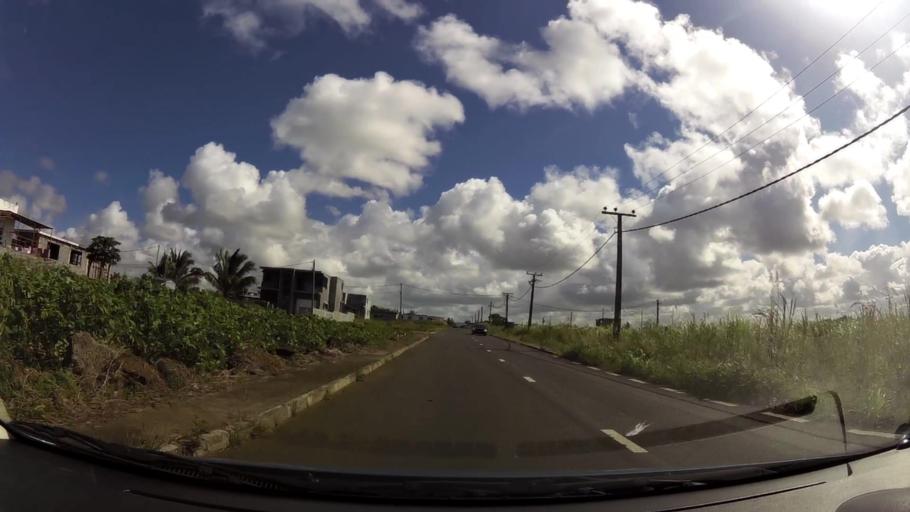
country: MU
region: Grand Port
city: Plaine Magnien
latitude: -20.4377
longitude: 57.6682
